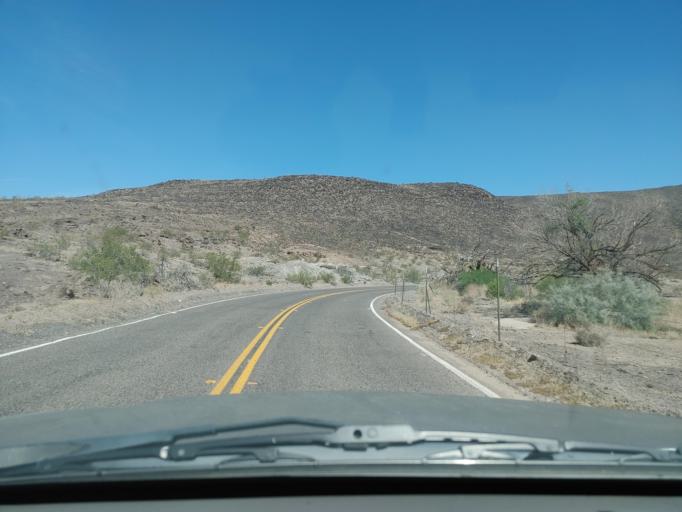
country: US
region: Arizona
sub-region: Maricopa County
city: Gila Bend
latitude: 32.9850
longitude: -113.3243
